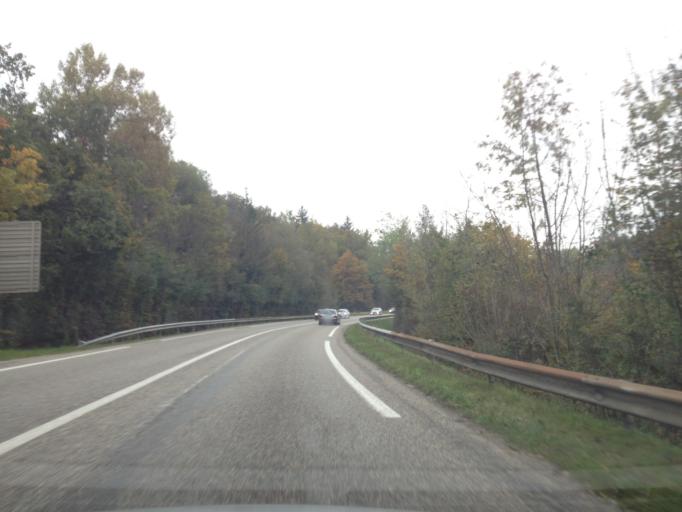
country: FR
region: Rhone-Alpes
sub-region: Departement de la Haute-Savoie
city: Seynod
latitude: 45.8650
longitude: 6.0697
